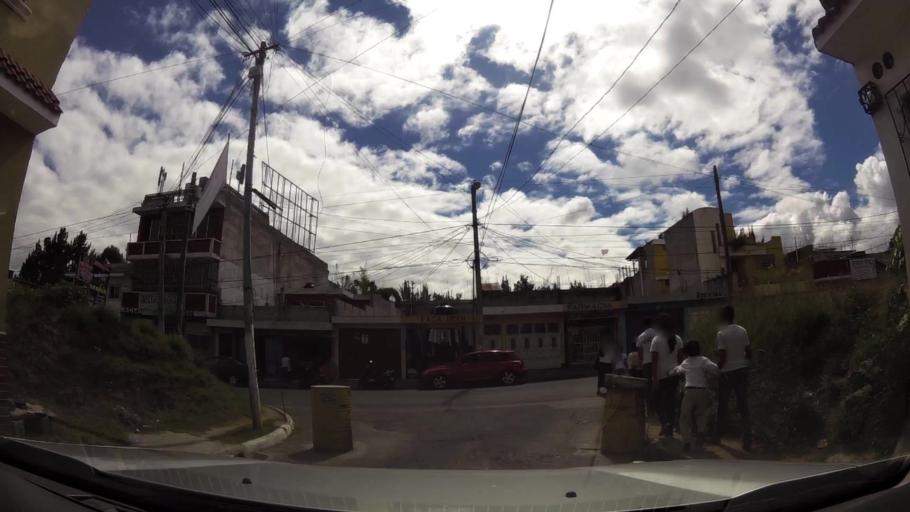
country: GT
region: Guatemala
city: Guatemala City
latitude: 14.6812
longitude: -90.5455
